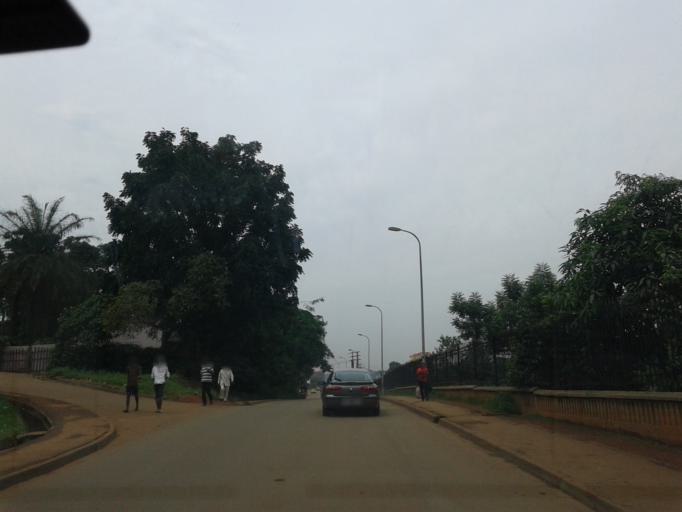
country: CM
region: Centre
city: Yaounde
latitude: 3.8591
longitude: 11.5223
